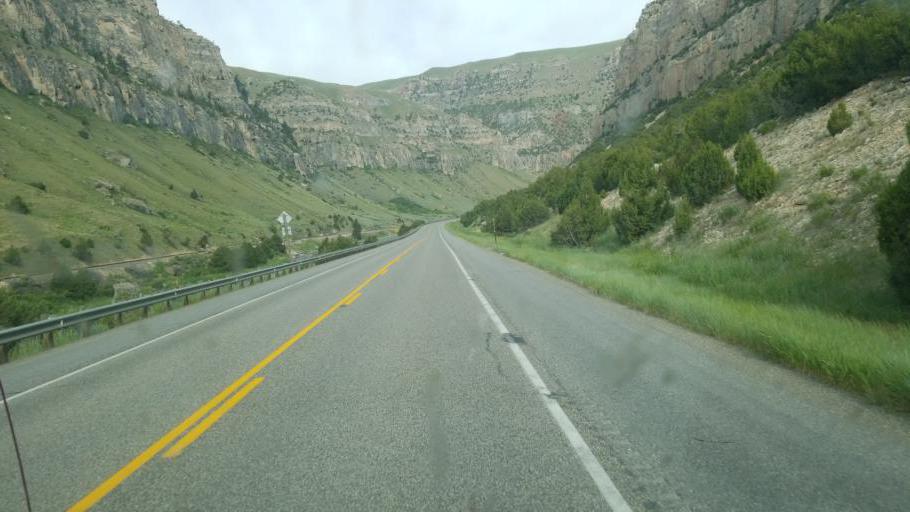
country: US
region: Wyoming
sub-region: Hot Springs County
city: Thermopolis
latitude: 43.5078
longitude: -108.1715
